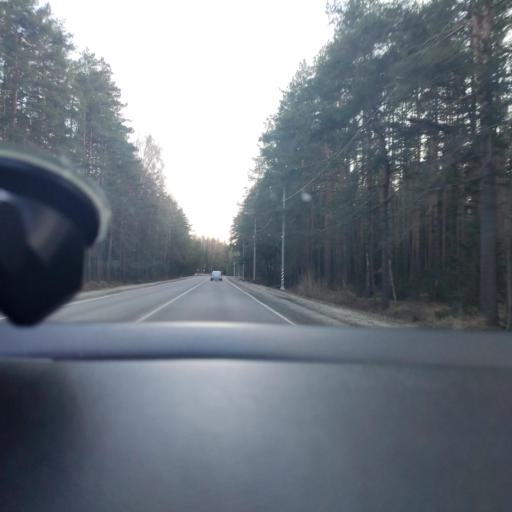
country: RU
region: Moskovskaya
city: Krasnyy Tkach
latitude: 55.4129
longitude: 39.1715
